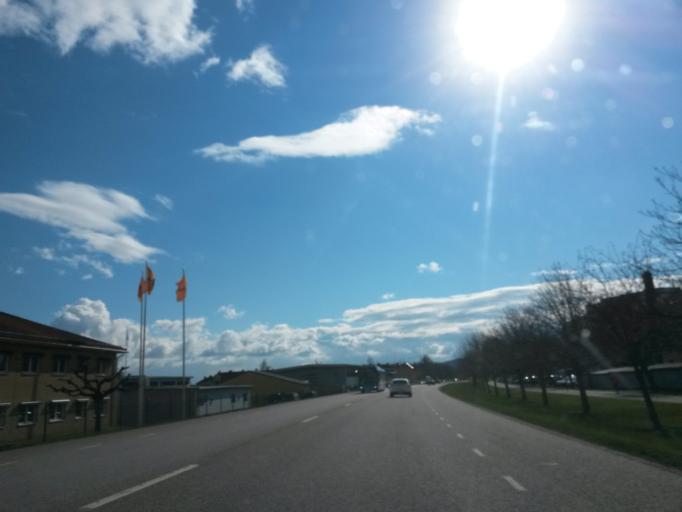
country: SE
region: Vaestra Goetaland
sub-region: Skovde Kommun
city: Skoevde
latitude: 58.4029
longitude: 13.8492
